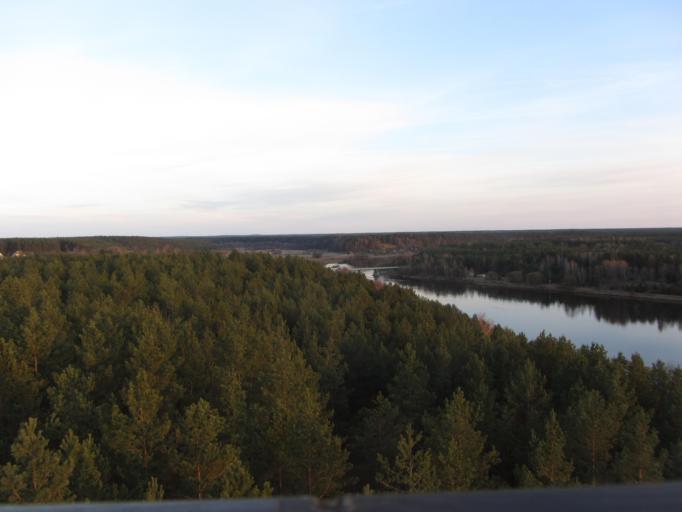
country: LT
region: Alytaus apskritis
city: Druskininkai
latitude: 54.1638
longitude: 24.1753
